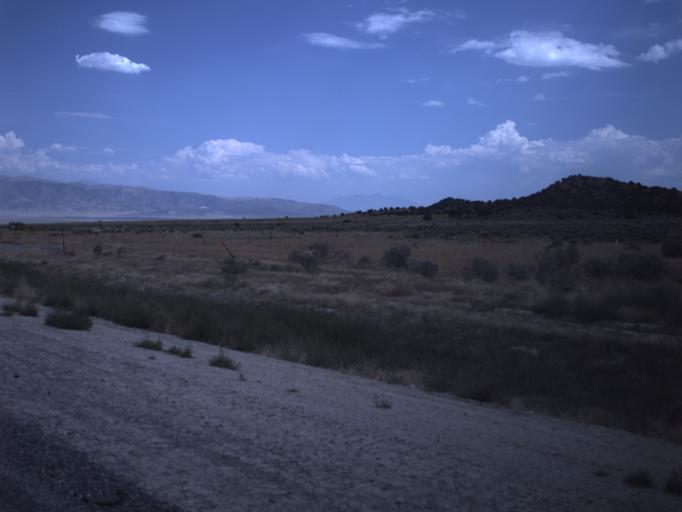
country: US
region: Utah
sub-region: Utah County
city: Eagle Mountain
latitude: 40.2358
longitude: -112.1649
